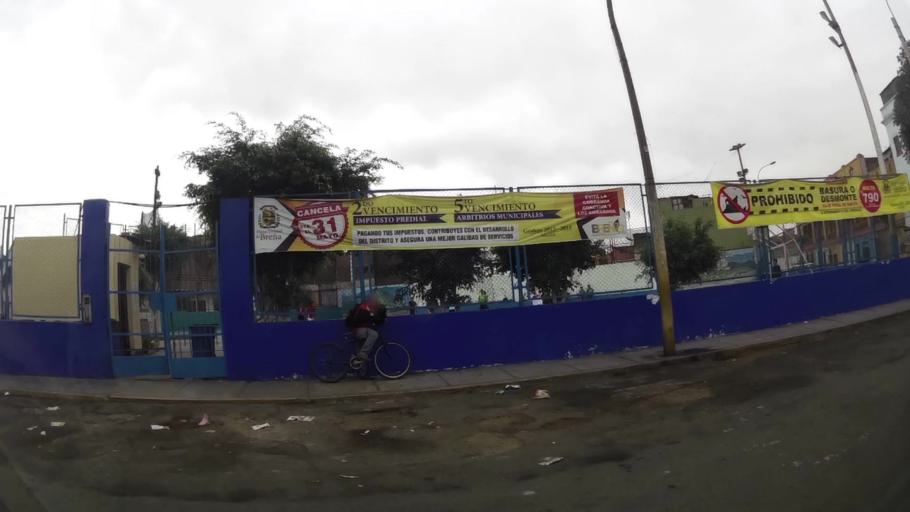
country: PE
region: Lima
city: Lima
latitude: -12.0525
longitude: -77.0511
